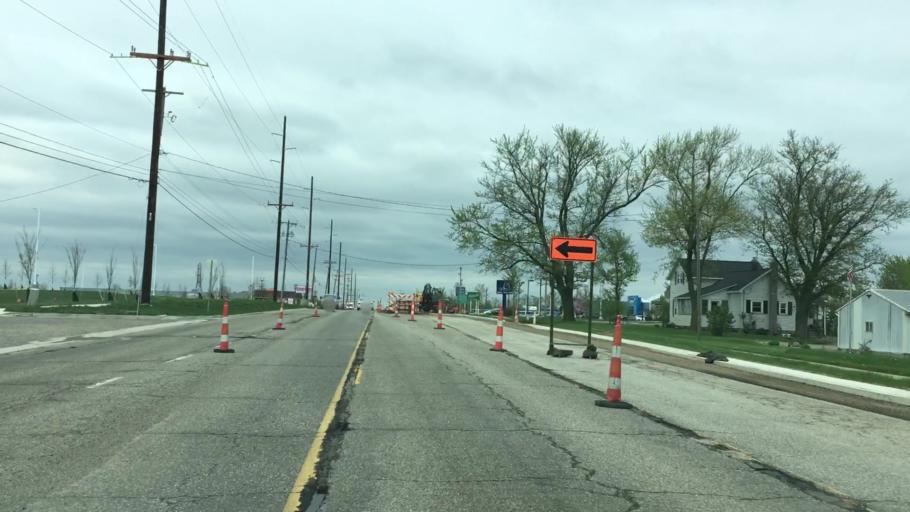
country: US
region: Michigan
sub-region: Ottawa County
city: Hudsonville
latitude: 42.8412
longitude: -85.8618
